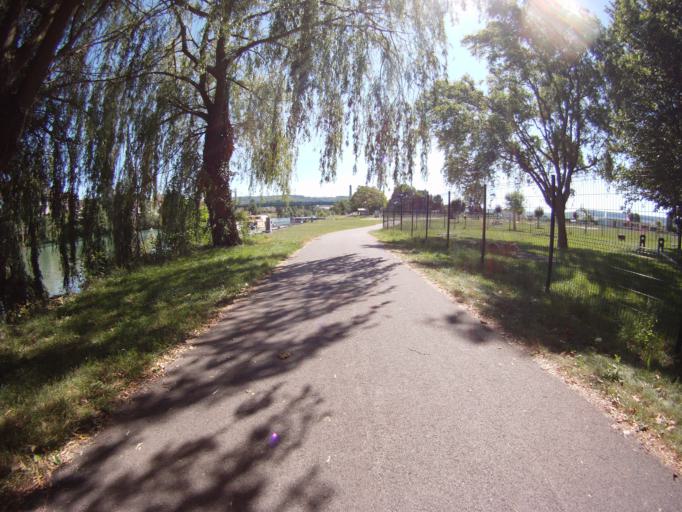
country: FR
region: Champagne-Ardenne
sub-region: Departement de la Marne
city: Dormans
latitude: 49.0772
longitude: 3.6382
